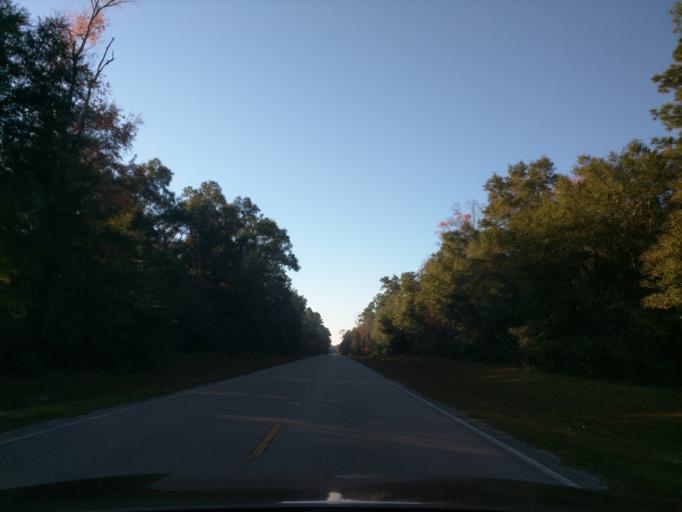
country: US
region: Florida
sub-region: Leon County
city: Woodville
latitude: 30.2776
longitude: -84.1611
